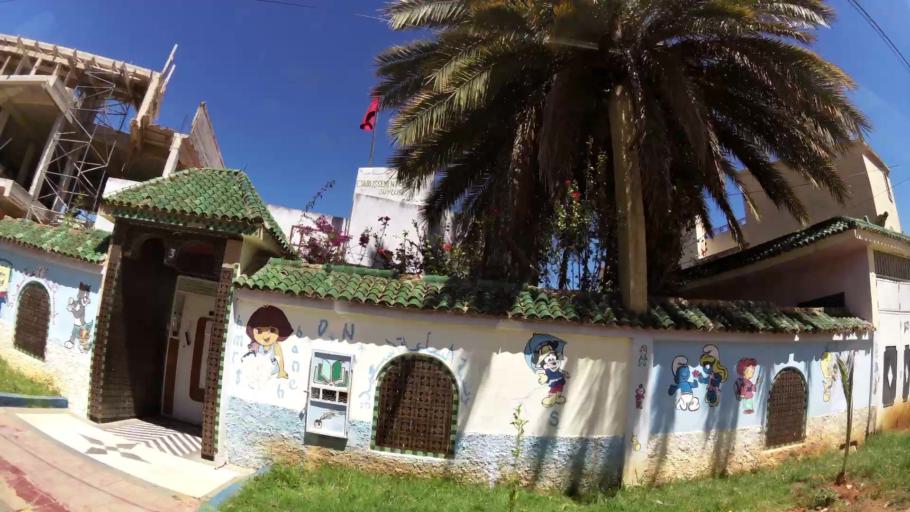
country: MA
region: Meknes-Tafilalet
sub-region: Meknes
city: Meknes
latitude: 33.8881
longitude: -5.5449
